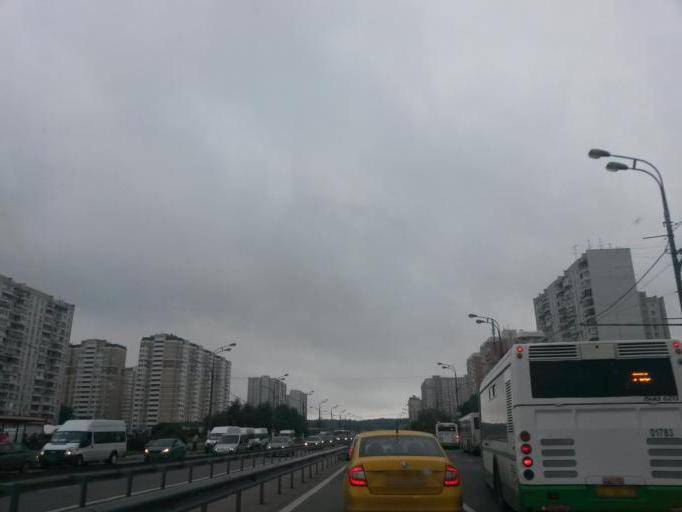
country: RU
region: Moscow
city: Annino
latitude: 55.5703
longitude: 37.5768
